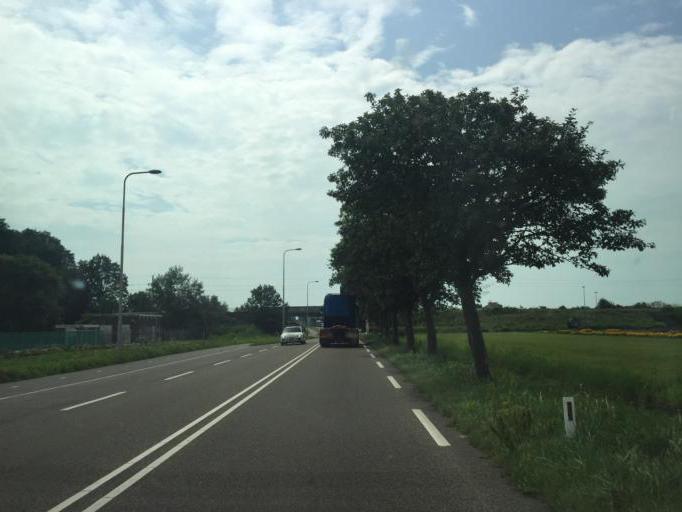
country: NL
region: North Holland
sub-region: Gemeente Enkhuizen
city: Enkhuizen
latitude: 52.6993
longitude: 5.2738
